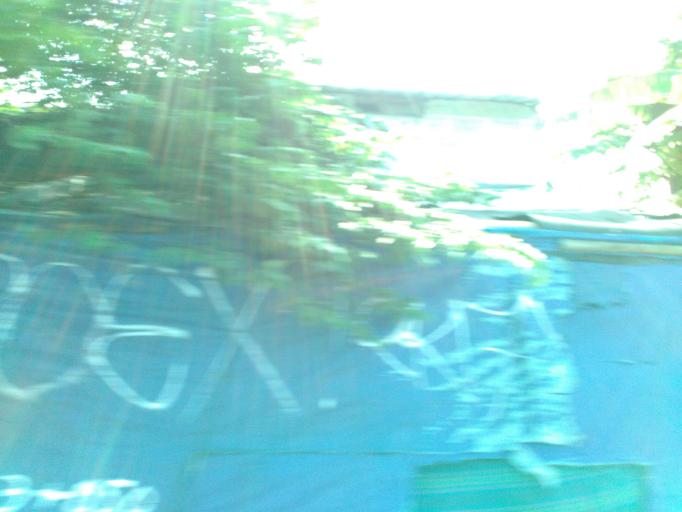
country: ID
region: Central Java
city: Delanggu
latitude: -7.6425
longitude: 110.6893
